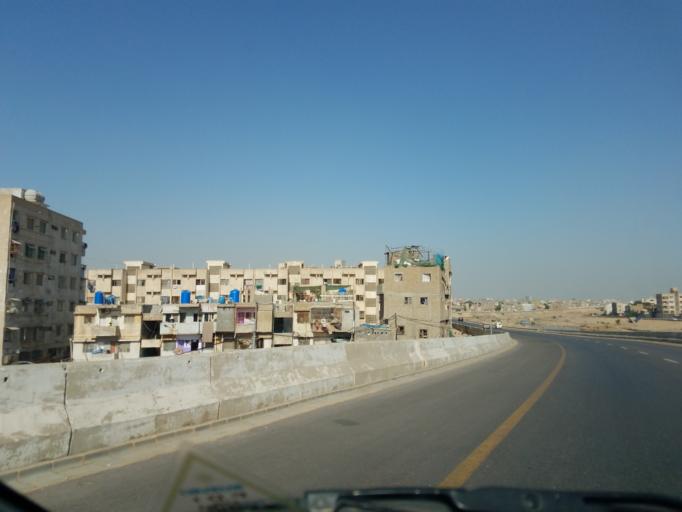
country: PK
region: Sindh
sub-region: Karachi District
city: Karachi
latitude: 24.8910
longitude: 67.0325
